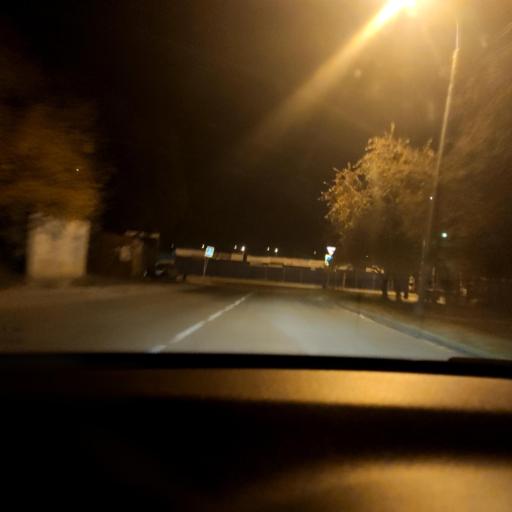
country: RU
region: Samara
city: Petra-Dubrava
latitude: 53.2286
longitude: 50.2810
